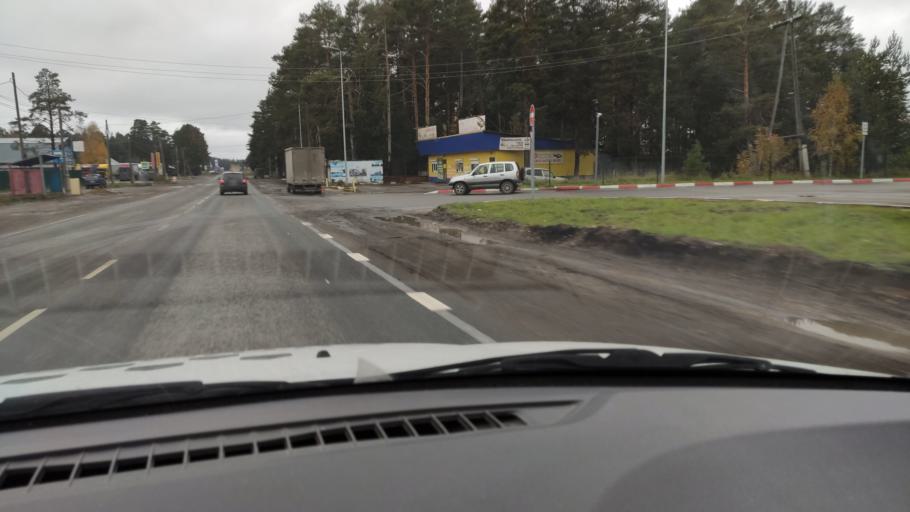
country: RU
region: Kirov
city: Belaya Kholunitsa
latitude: 58.8473
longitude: 50.8225
